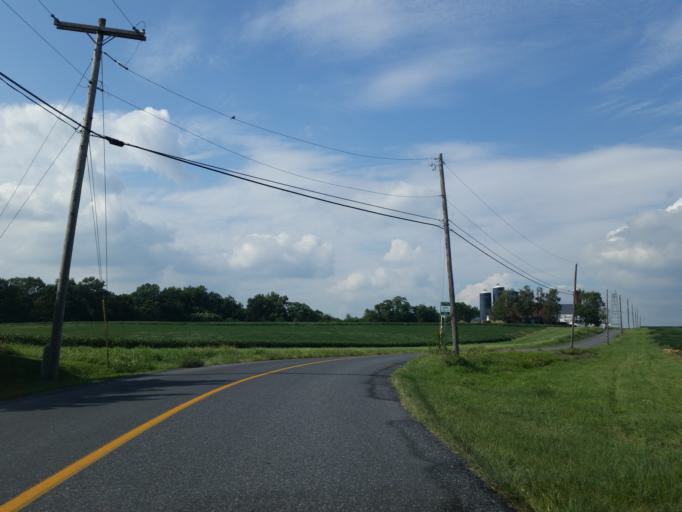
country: US
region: Pennsylvania
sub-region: Lancaster County
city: Mount Joy
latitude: 40.1286
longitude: -76.4677
